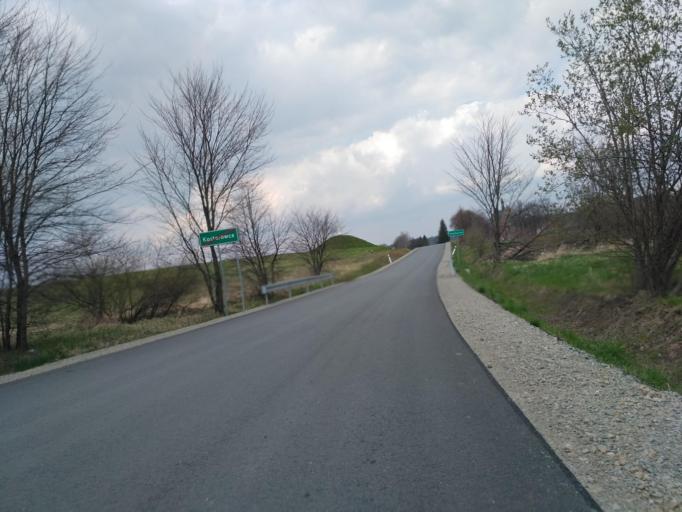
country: PL
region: Subcarpathian Voivodeship
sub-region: Powiat sanocki
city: Strachocina
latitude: 49.5957
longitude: 22.0989
